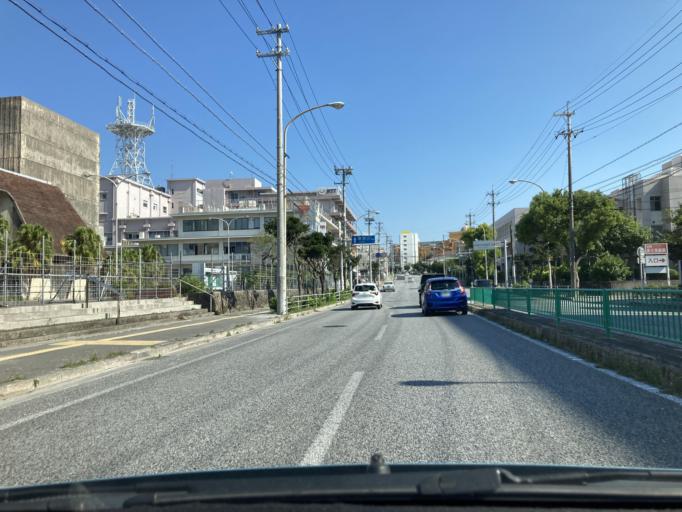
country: JP
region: Okinawa
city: Naha-shi
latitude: 26.2073
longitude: 127.6930
